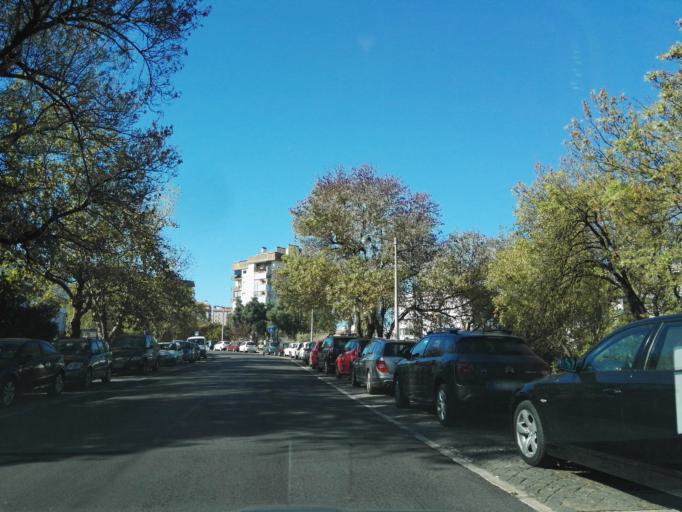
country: PT
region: Lisbon
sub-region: Loures
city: Moscavide
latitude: 38.7768
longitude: -9.1148
